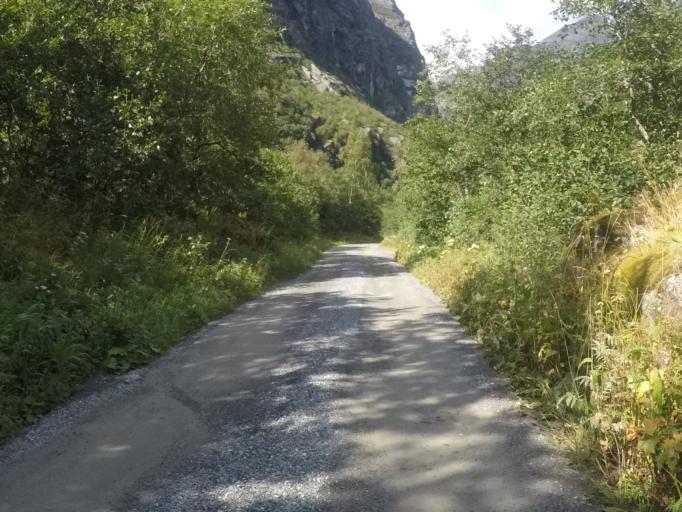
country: NO
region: Sogn og Fjordane
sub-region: Stryn
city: Stryn
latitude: 61.7477
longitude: 7.0350
